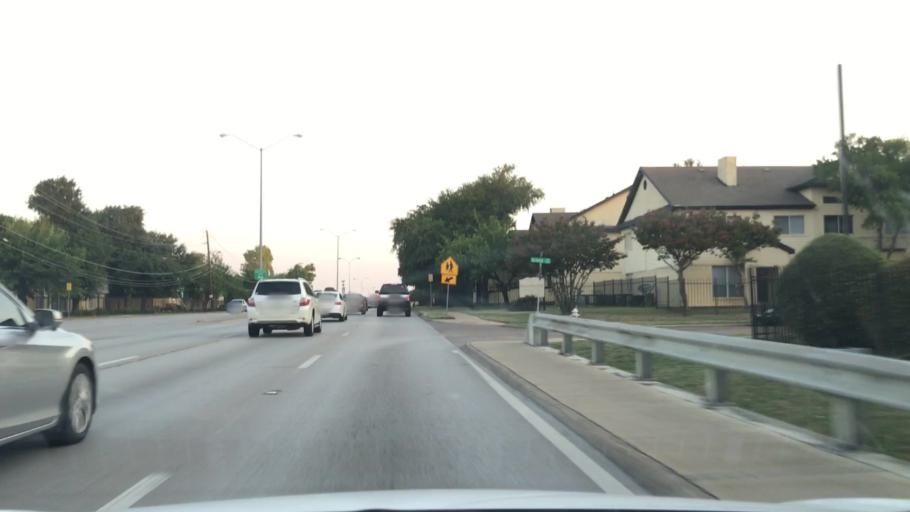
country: US
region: Texas
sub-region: Dallas County
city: Mesquite
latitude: 32.8150
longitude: -96.6878
